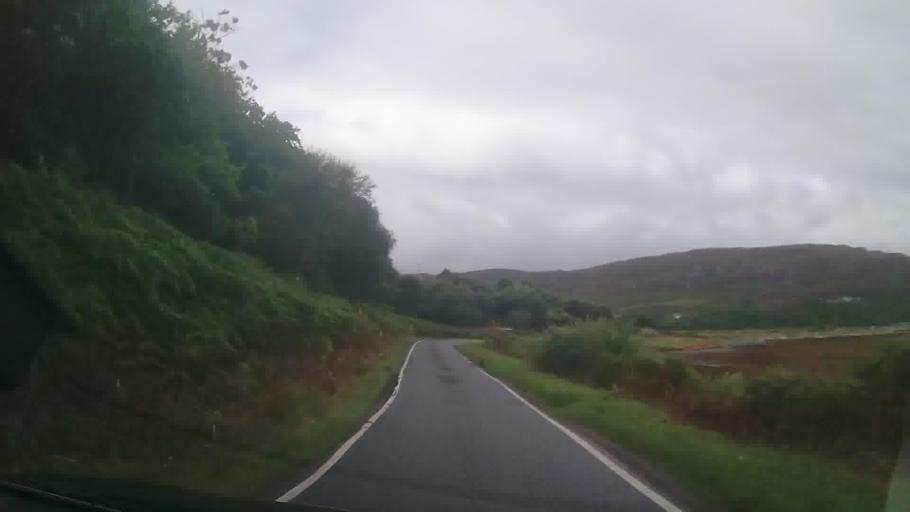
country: GB
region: Scotland
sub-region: Argyll and Bute
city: Isle Of Mull
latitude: 56.6866
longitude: -5.9495
